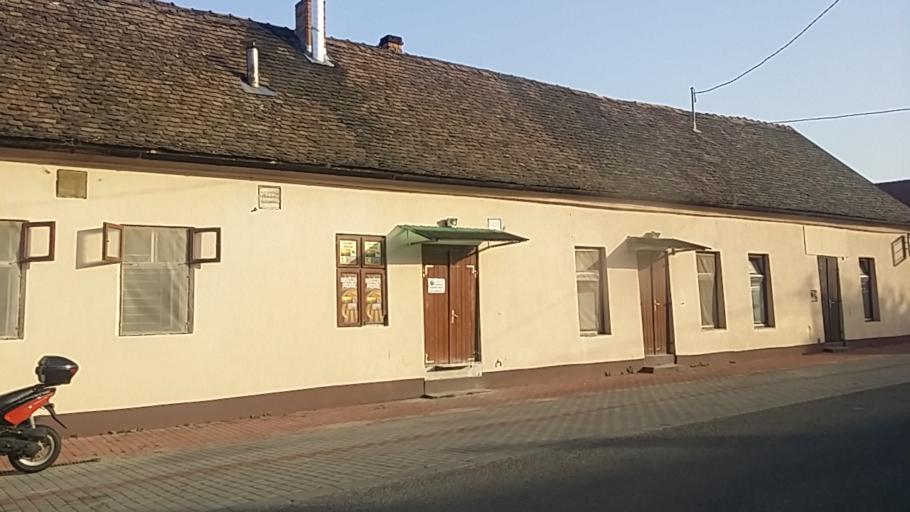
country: HU
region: Baranya
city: Villany
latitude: 45.8667
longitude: 18.4509
